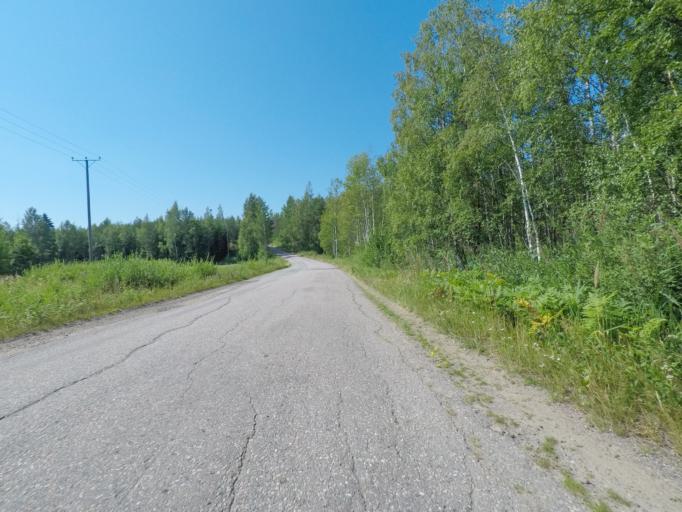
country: FI
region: Southern Savonia
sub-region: Mikkeli
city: Puumala
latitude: 61.4235
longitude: 28.1526
